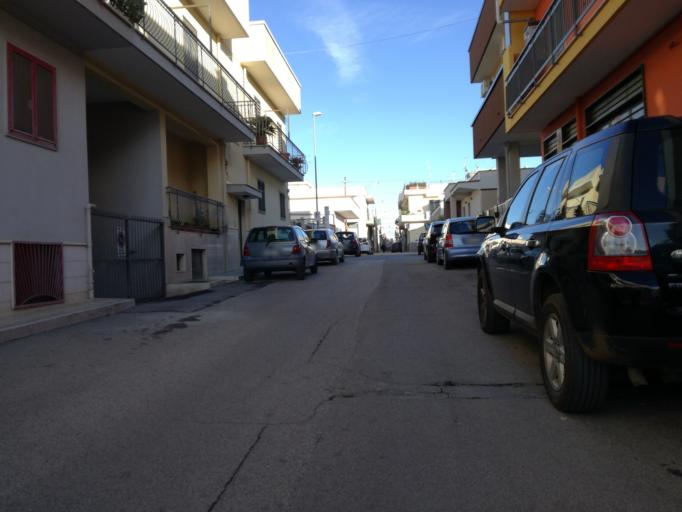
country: IT
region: Apulia
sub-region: Provincia di Bari
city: Adelfia
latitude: 41.0014
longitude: 16.8640
